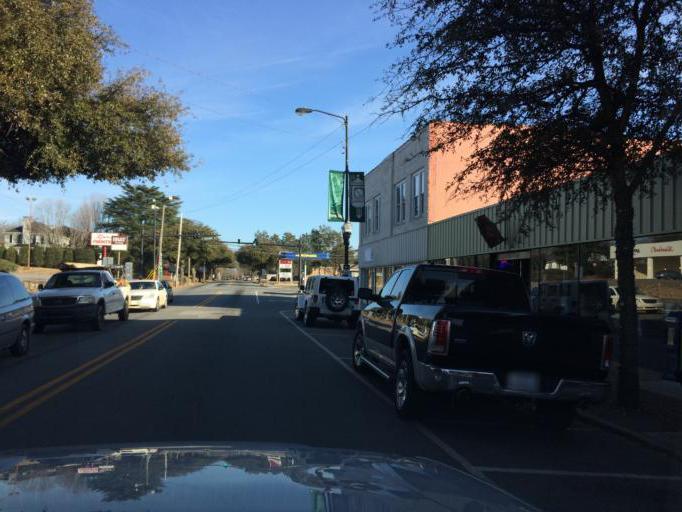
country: US
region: North Carolina
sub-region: Rutherford County
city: Forest City
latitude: 35.3332
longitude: -81.8629
